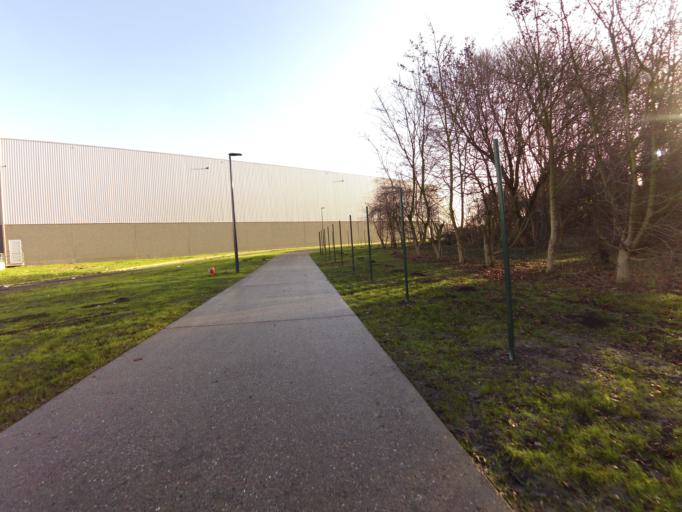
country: BE
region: Flanders
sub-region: Provincie West-Vlaanderen
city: Ostend
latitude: 51.2124
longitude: 2.9558
